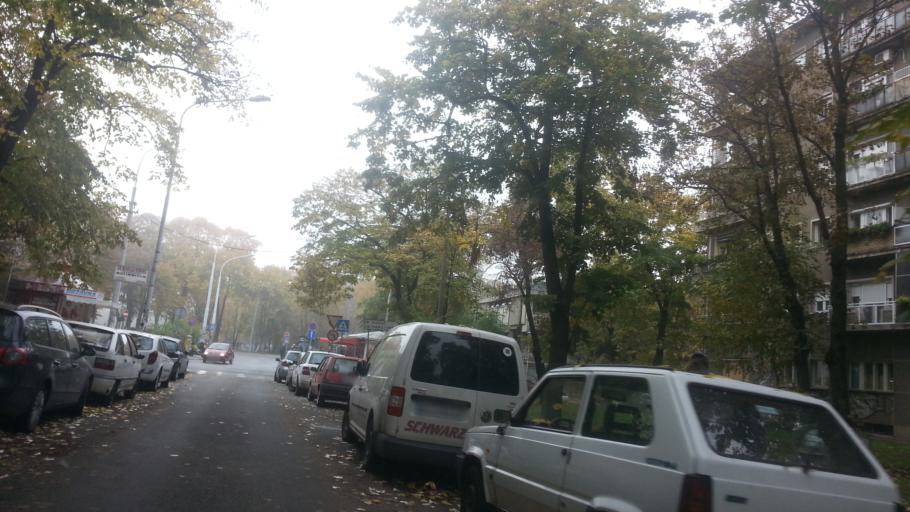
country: RS
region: Central Serbia
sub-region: Belgrade
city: Zemun
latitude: 44.8308
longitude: 20.4042
